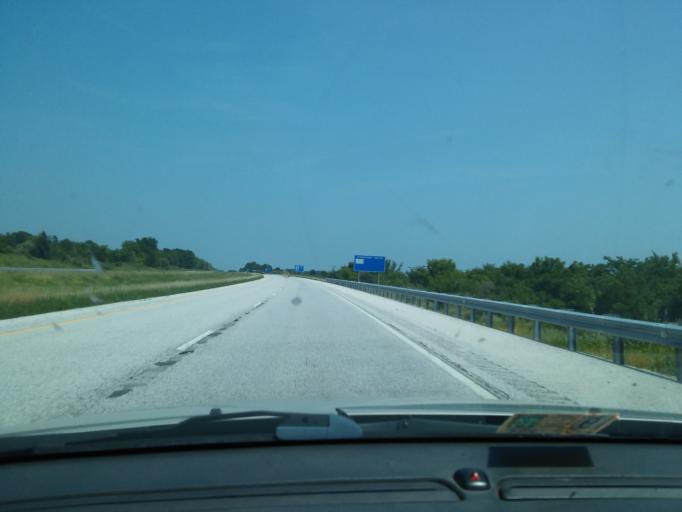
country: US
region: Illinois
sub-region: Morgan County
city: South Jacksonville
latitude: 39.6807
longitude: -90.2652
